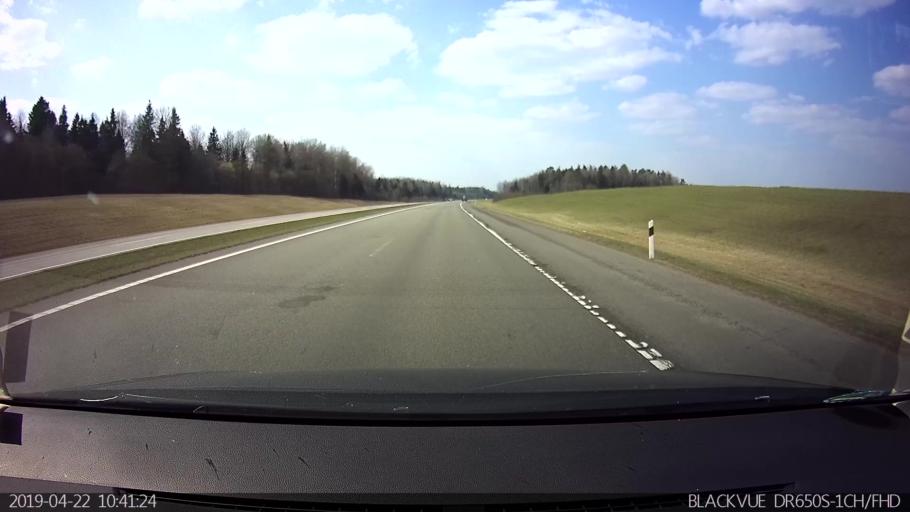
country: BY
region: Vitebsk
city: Talachyn
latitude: 54.4103
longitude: 29.4994
